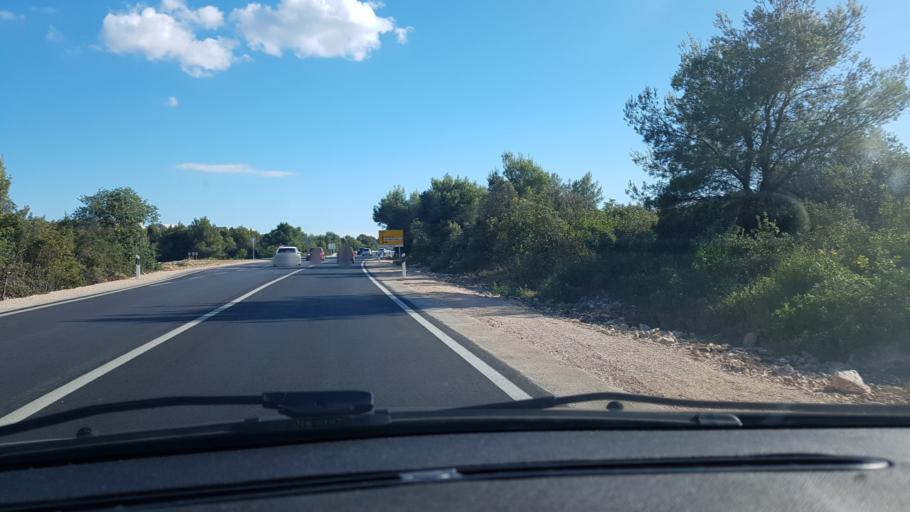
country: HR
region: Sibensko-Kniniska
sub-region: Grad Sibenik
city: Brodarica
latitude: 43.7013
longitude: 15.9066
